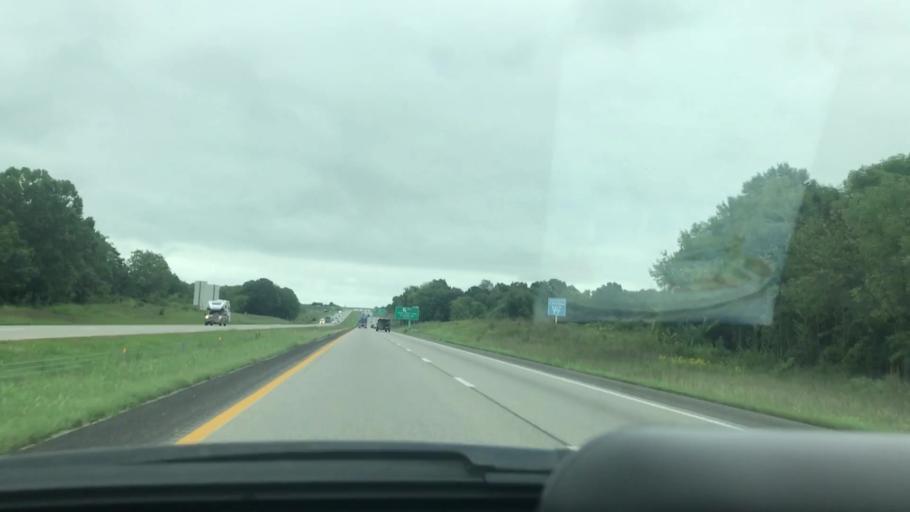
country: US
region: Missouri
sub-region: Greene County
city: Republic
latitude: 37.1927
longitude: -93.4603
